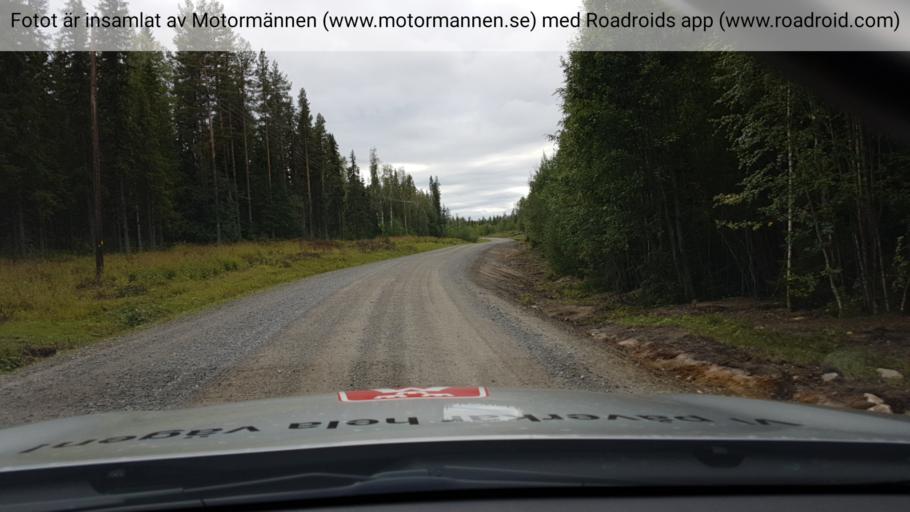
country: SE
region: Jaemtland
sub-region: Ragunda Kommun
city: Hammarstrand
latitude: 62.9179
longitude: 16.1062
